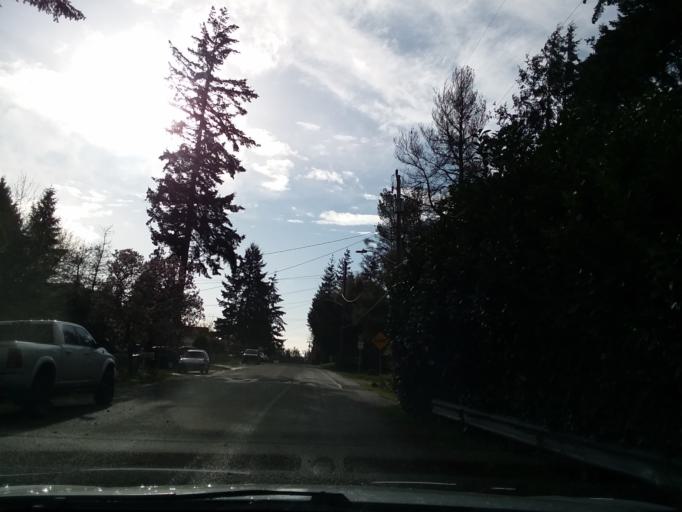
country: US
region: Washington
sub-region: King County
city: Lake Forest Park
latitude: 47.7576
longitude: -122.3088
